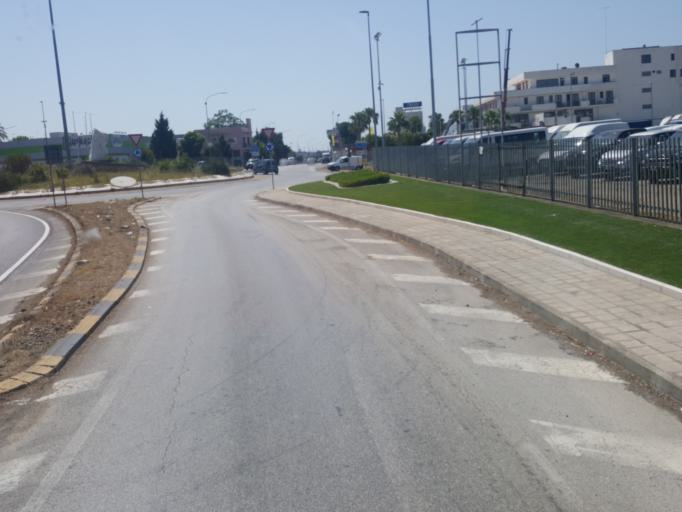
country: IT
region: Apulia
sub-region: Provincia di Taranto
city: Massafra
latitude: 40.5832
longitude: 17.1114
